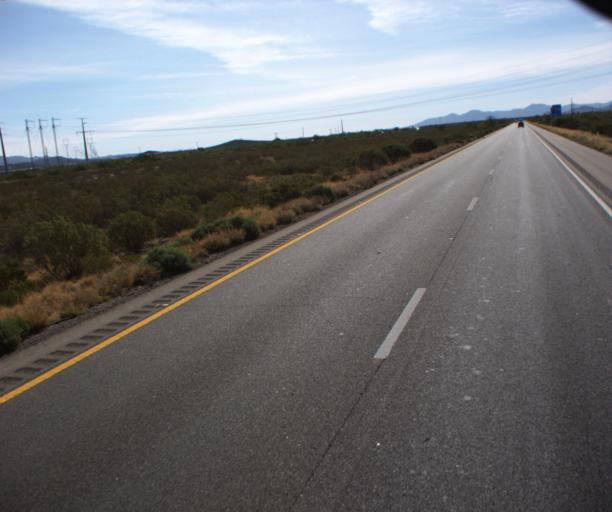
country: US
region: Arizona
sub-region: Pima County
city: Vail
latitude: 32.0341
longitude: -110.7312
